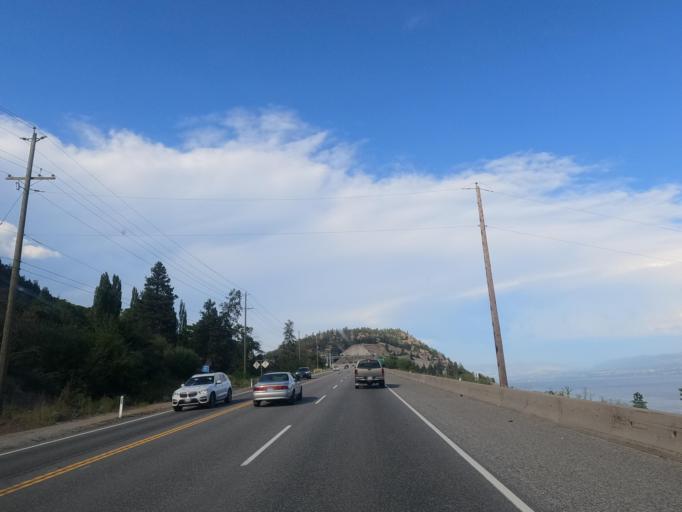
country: CA
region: British Columbia
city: Peachland
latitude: 49.8011
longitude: -119.6710
